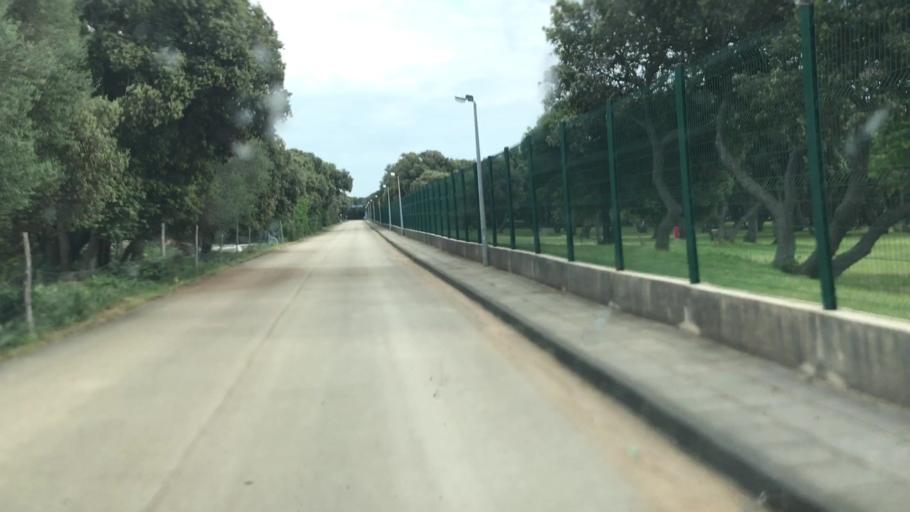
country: HR
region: Licko-Senjska
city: Novalja
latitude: 44.5420
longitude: 14.8846
